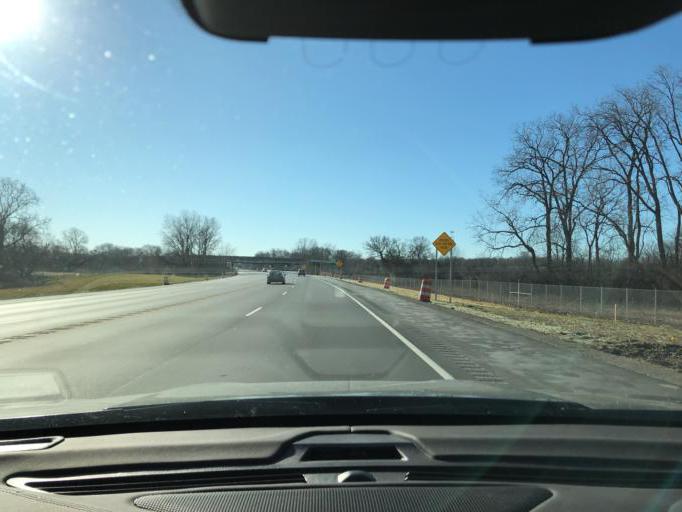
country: US
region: Michigan
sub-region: Washtenaw County
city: Ypsilanti
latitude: 42.2450
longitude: -83.5629
